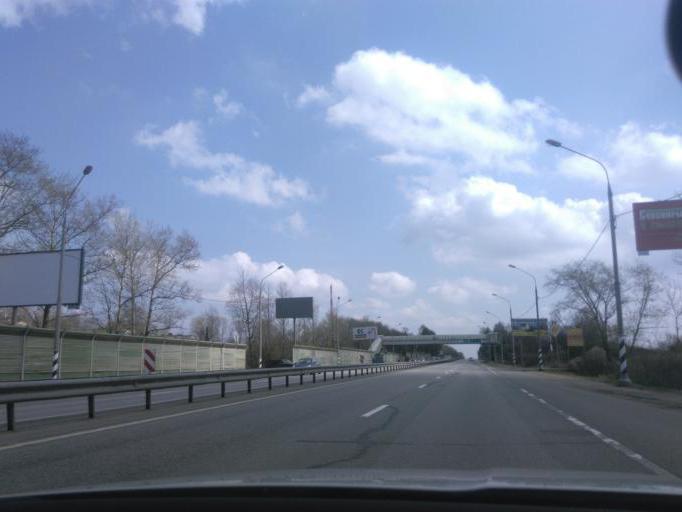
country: RU
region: Moskovskaya
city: Chashnikovo
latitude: 56.0285
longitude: 37.1711
